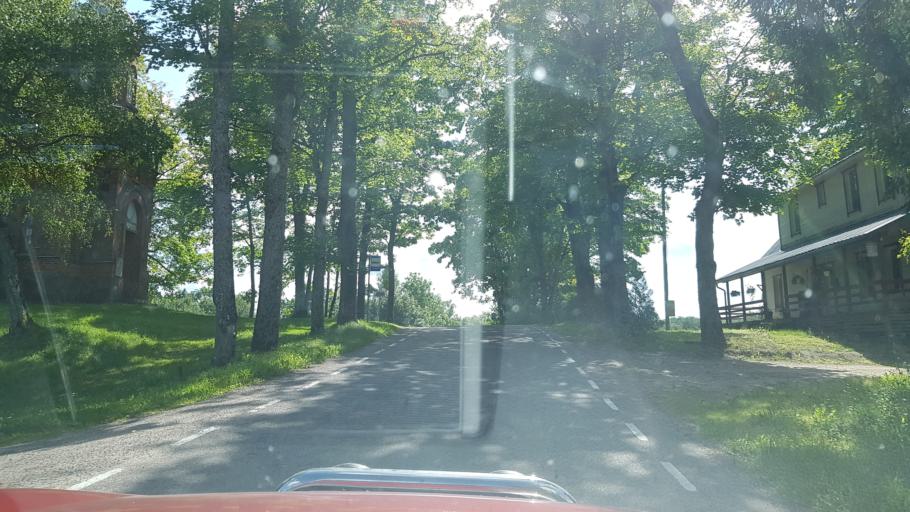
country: EE
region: Vorumaa
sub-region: Voru linn
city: Voru
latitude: 57.6733
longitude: 27.0821
